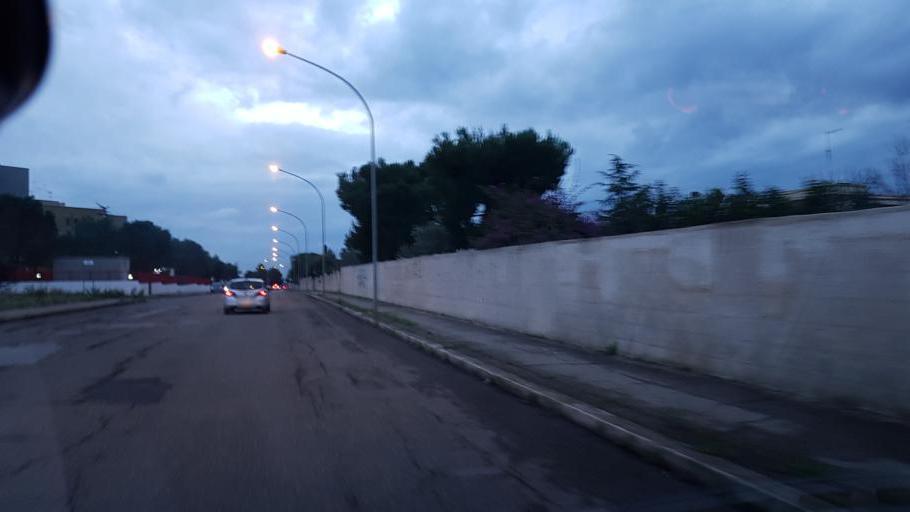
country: IT
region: Apulia
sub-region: Provincia di Taranto
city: Paolo VI
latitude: 40.5302
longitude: 17.2813
